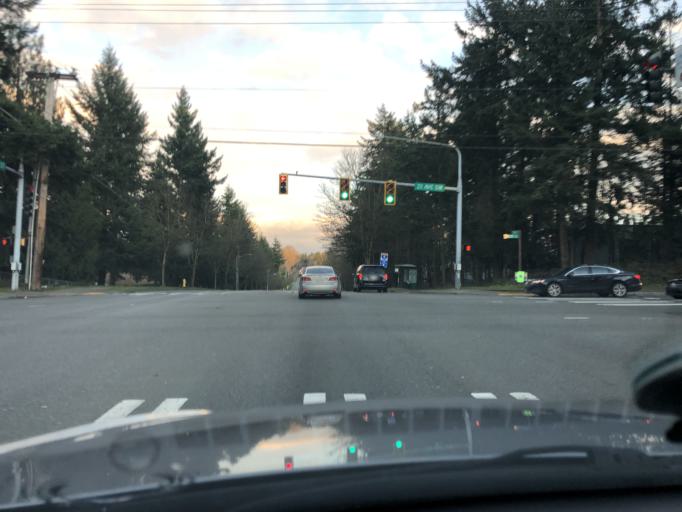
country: US
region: Washington
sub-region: King County
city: Federal Way
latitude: 47.3152
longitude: -122.3612
